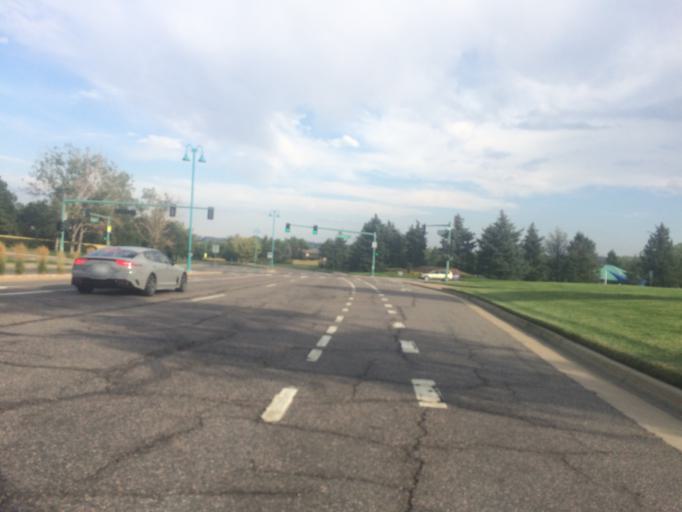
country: US
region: Colorado
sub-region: Boulder County
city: Superior
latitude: 39.9401
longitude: -105.1563
